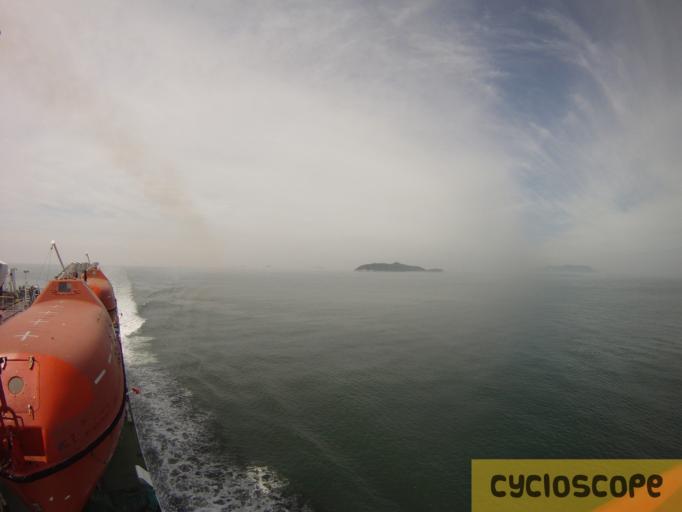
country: KR
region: Chungcheongnam-do
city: Taesal-li
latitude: 37.2806
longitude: 126.4255
